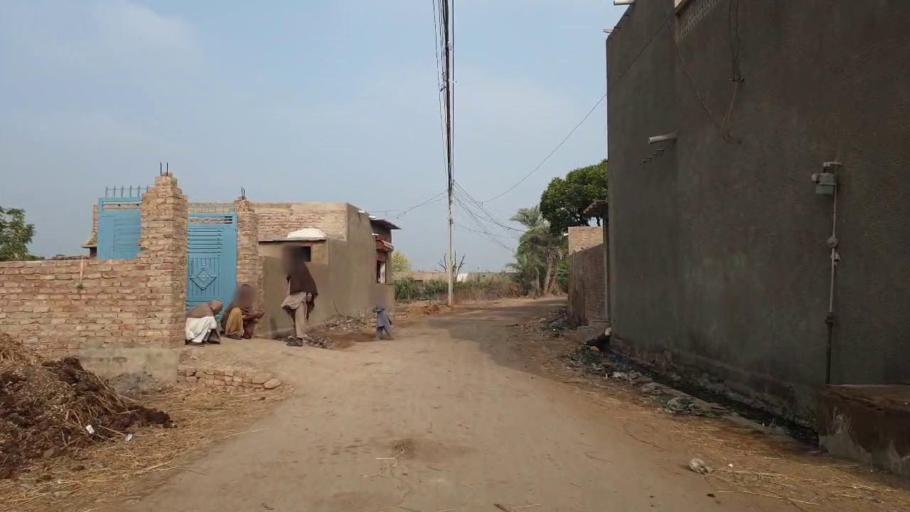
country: PK
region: Sindh
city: Tando Muhammad Khan
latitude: 25.1293
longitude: 68.5917
